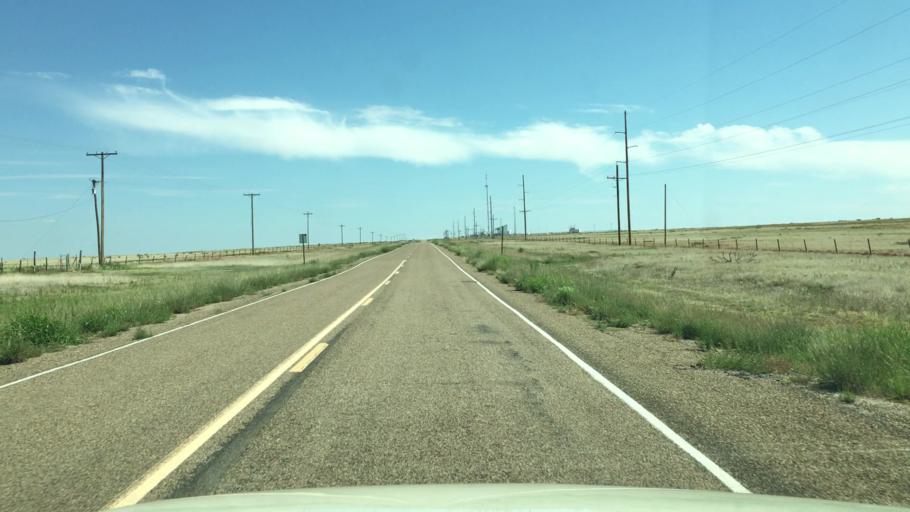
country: US
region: New Mexico
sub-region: Chaves County
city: Roswell
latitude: 33.9542
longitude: -104.5866
